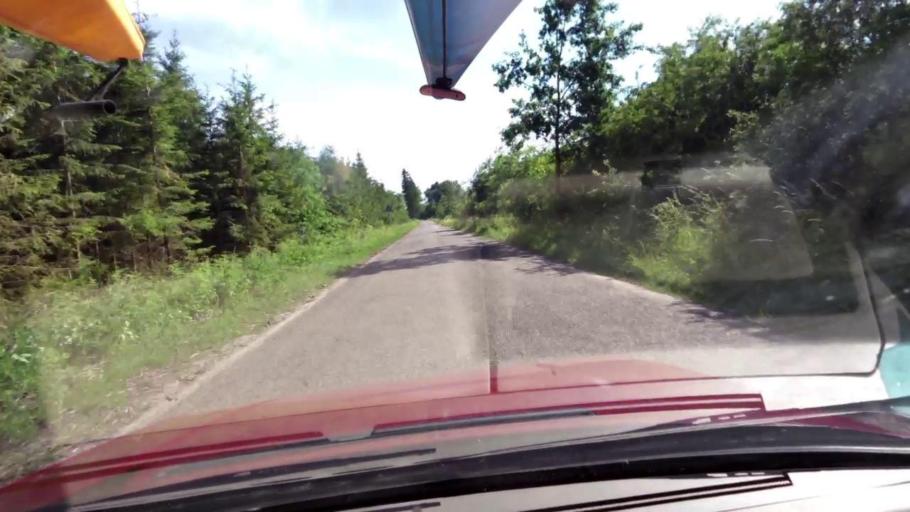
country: PL
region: Pomeranian Voivodeship
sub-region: Powiat slupski
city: Kepice
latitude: 54.1840
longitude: 16.8887
